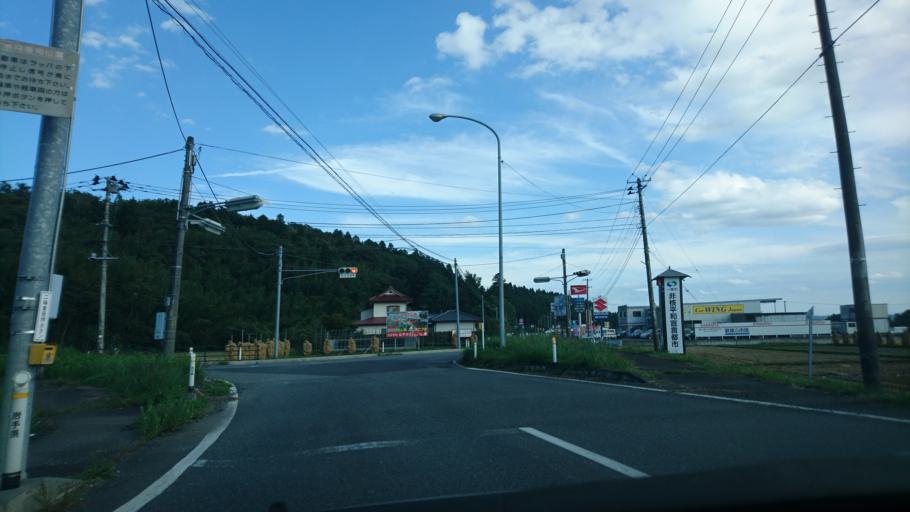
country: JP
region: Iwate
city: Ichinoseki
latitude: 38.8624
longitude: 141.1519
